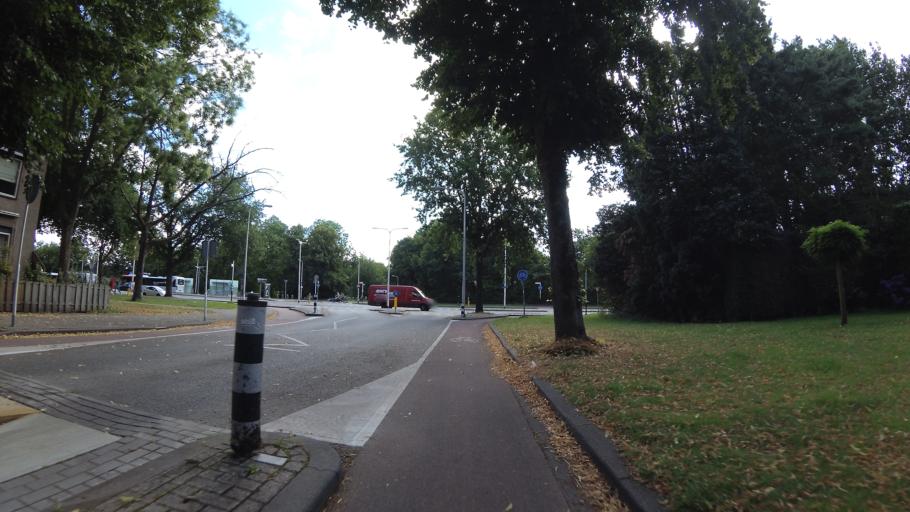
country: NL
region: North Brabant
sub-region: Gemeente Tilburg
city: Tilburg
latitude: 51.5402
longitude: 5.1001
